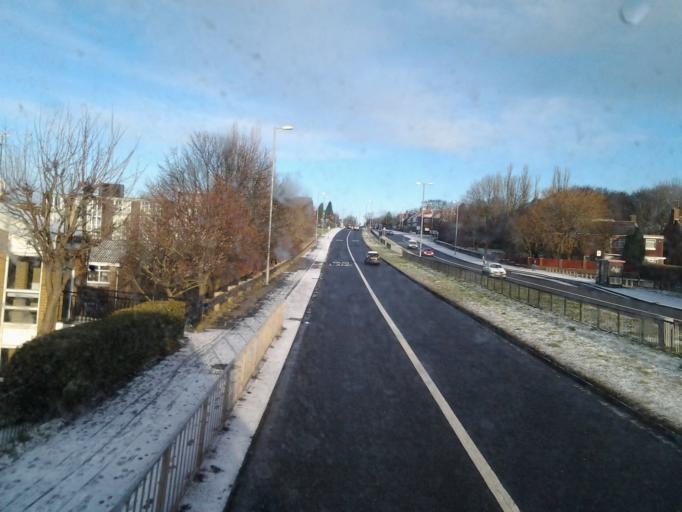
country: GB
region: England
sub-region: Gateshead
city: Lamesley
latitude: 54.9236
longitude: -1.5933
